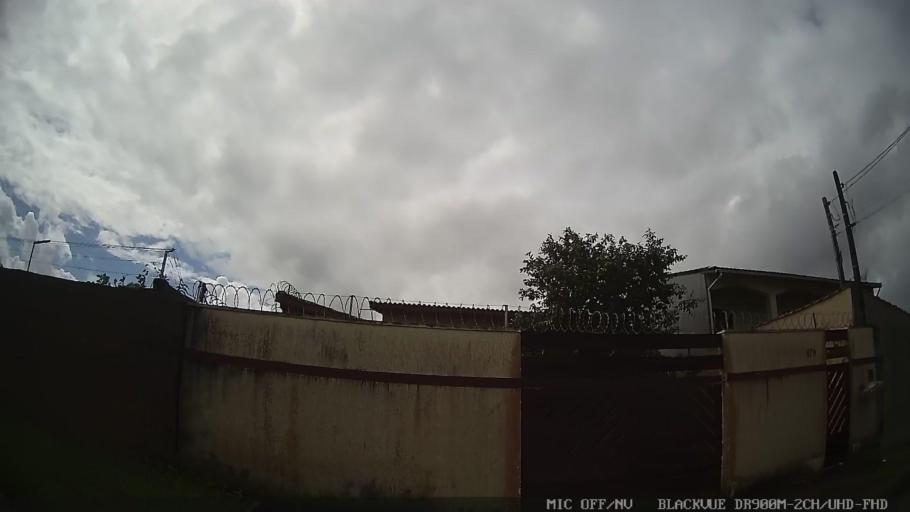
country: BR
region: Sao Paulo
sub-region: Itanhaem
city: Itanhaem
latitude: -24.1600
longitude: -46.7943
